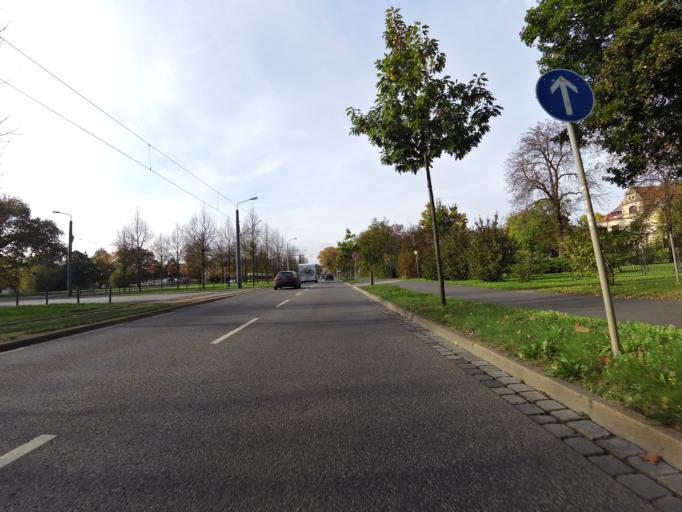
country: DE
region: Saxony
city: Dresden
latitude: 51.0433
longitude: 13.7628
